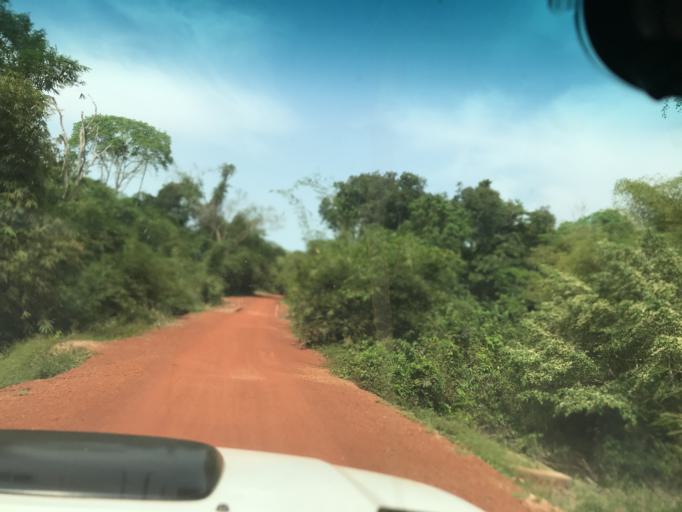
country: CD
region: Eastern Province
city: Buta
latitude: 2.8909
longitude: 24.3005
